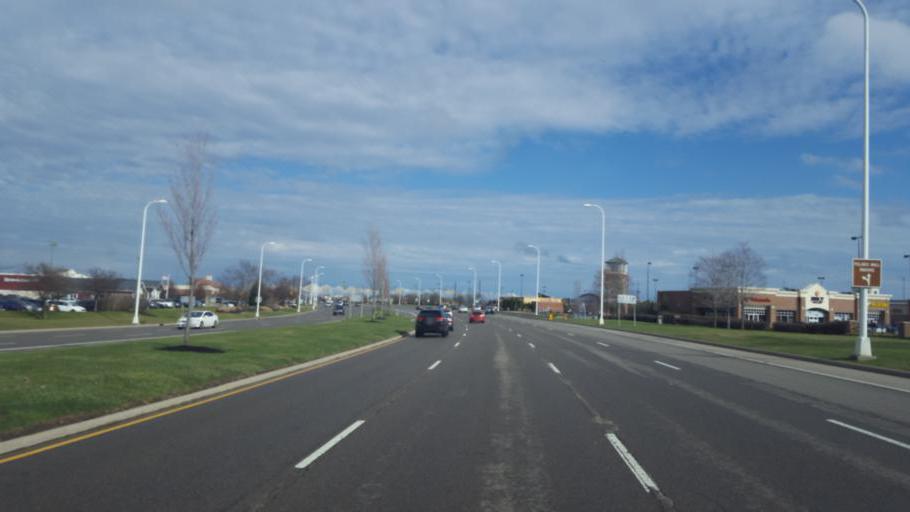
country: US
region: Ohio
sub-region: Franklin County
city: Worthington
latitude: 40.1421
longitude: -82.9877
